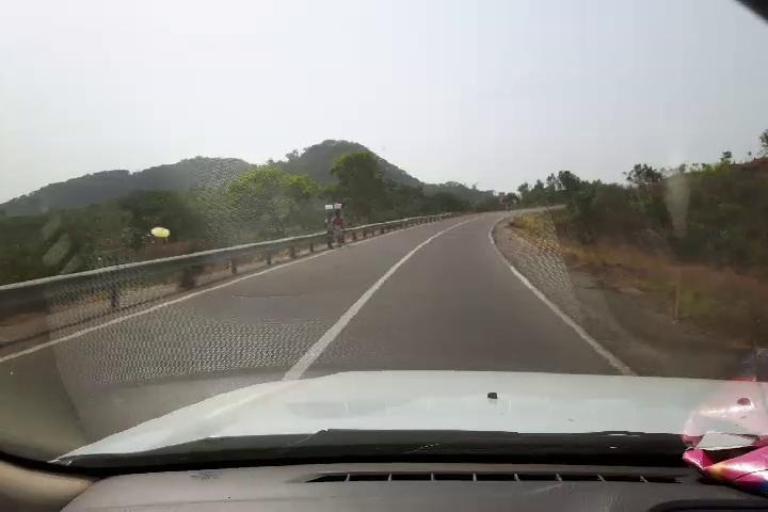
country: SL
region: Western Area
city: Waterloo
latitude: 8.2073
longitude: -13.1317
